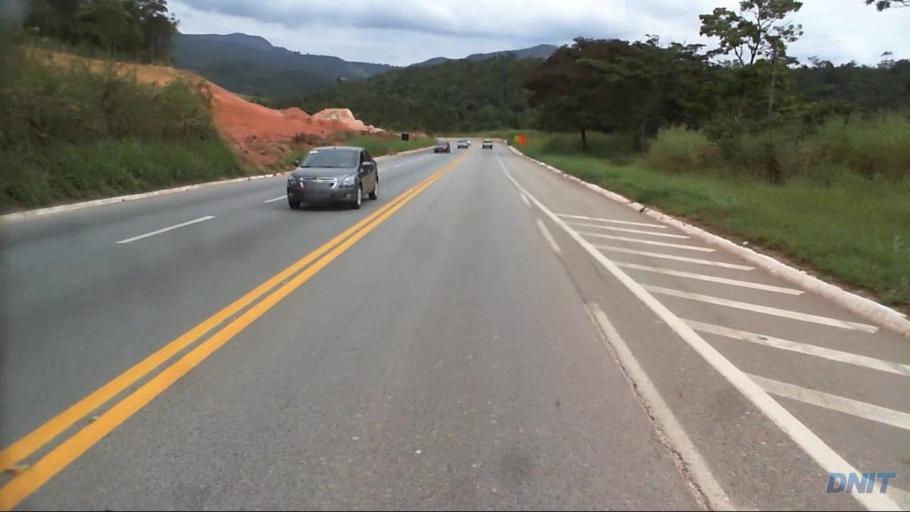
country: BR
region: Minas Gerais
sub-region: Caete
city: Caete
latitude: -19.7768
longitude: -43.6546
